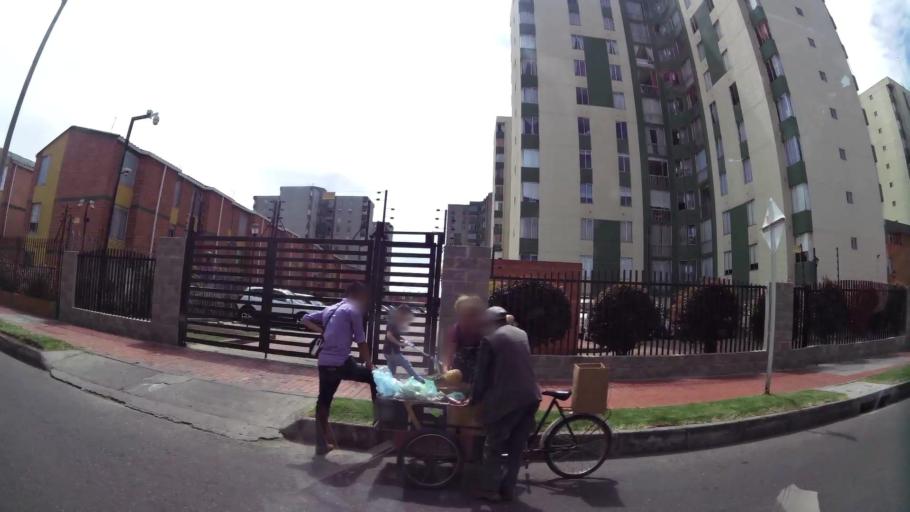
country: CO
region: Bogota D.C.
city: Bogota
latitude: 4.6188
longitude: -74.1296
